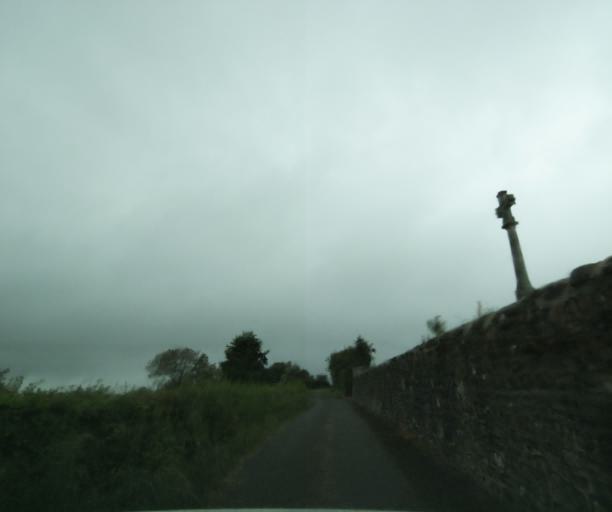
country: FR
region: Bourgogne
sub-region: Departement de Saone-et-Loire
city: Matour
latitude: 46.4319
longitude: 4.4720
